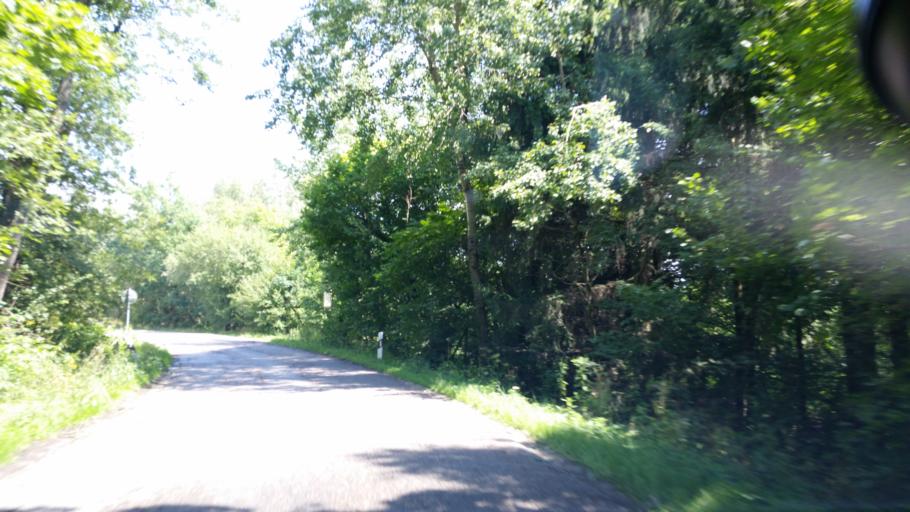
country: DE
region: Bavaria
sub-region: Lower Bavaria
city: Vilsbiburg
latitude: 48.4602
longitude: 12.3129
